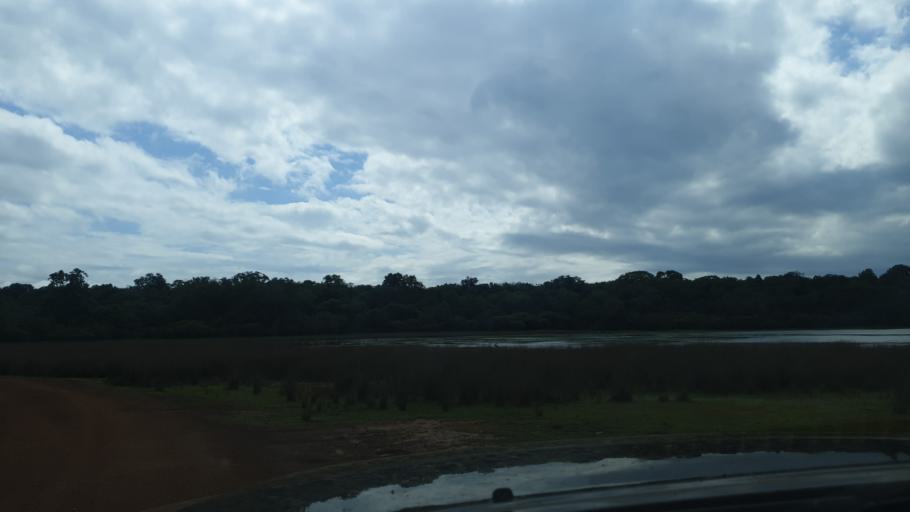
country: LK
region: North Central
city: Anuradhapura
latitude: 8.4251
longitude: 80.0236
